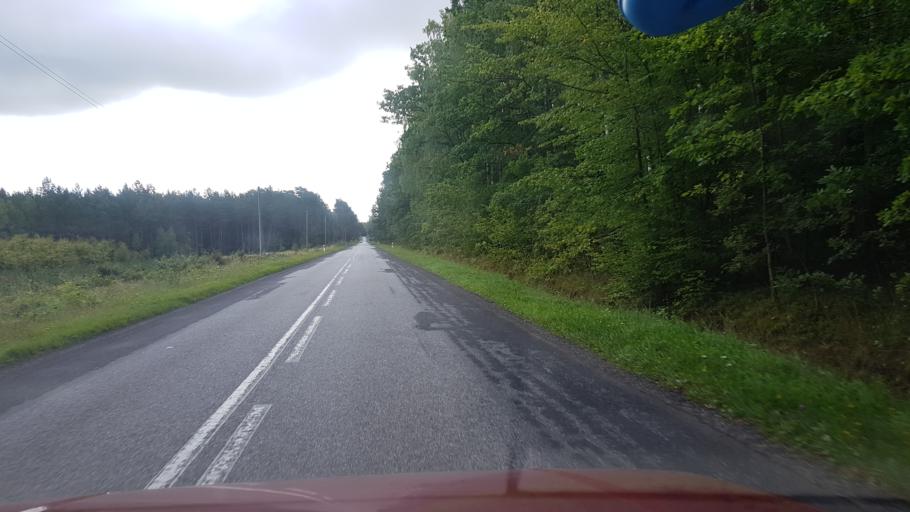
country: PL
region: West Pomeranian Voivodeship
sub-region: Powiat koszalinski
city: Polanow
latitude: 54.0996
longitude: 16.8147
